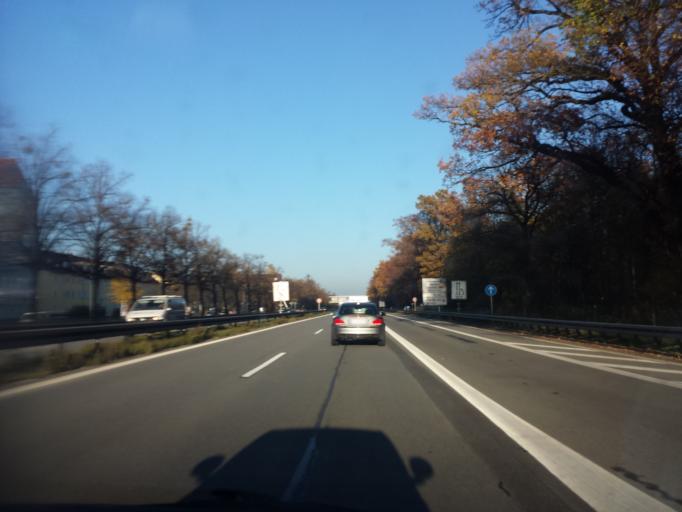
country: DE
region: Bavaria
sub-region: Upper Bavaria
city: Neuried
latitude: 48.1042
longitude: 11.5053
